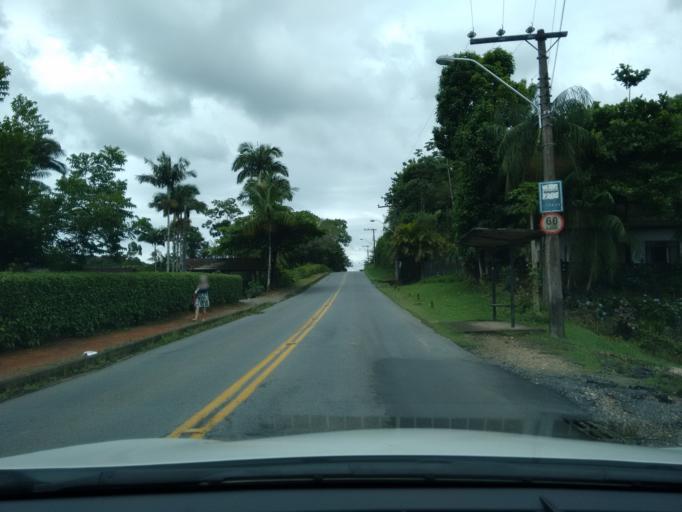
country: BR
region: Santa Catarina
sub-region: Blumenau
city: Blumenau
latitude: -26.8671
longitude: -49.1429
